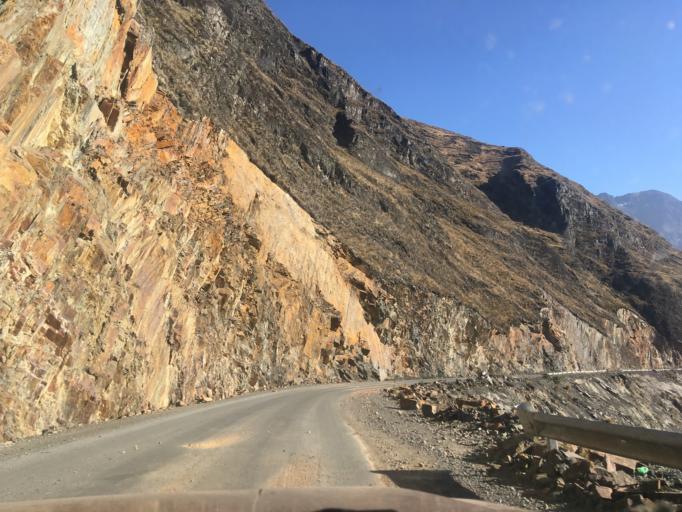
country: BO
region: La Paz
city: Quime
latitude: -17.0123
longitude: -67.2759
